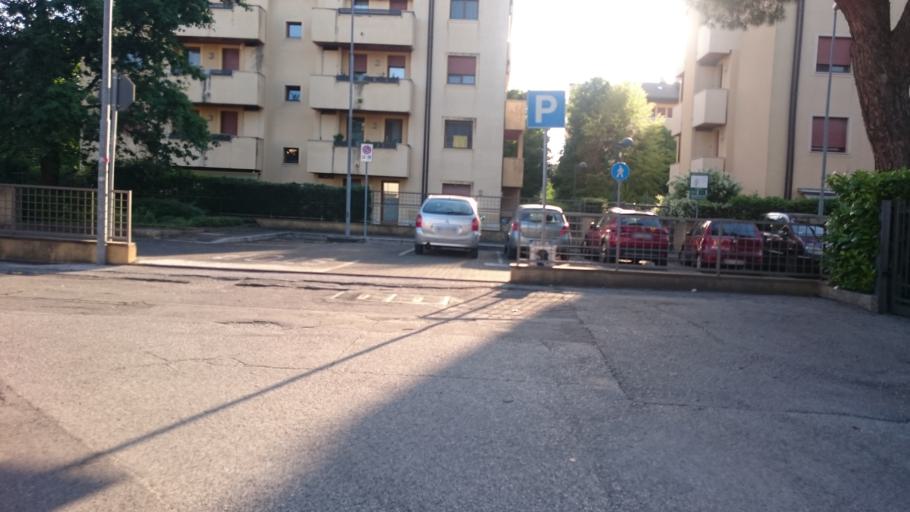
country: IT
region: Veneto
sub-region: Provincia di Padova
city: Padova
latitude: 45.4016
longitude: 11.8973
